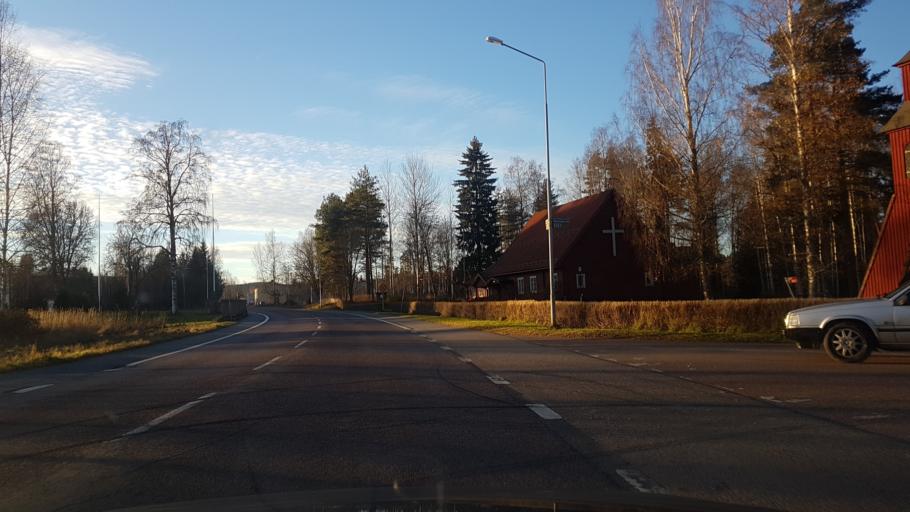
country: SE
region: Dalarna
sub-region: Faluns Kommun
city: Bjursas
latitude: 60.7134
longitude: 15.2977
